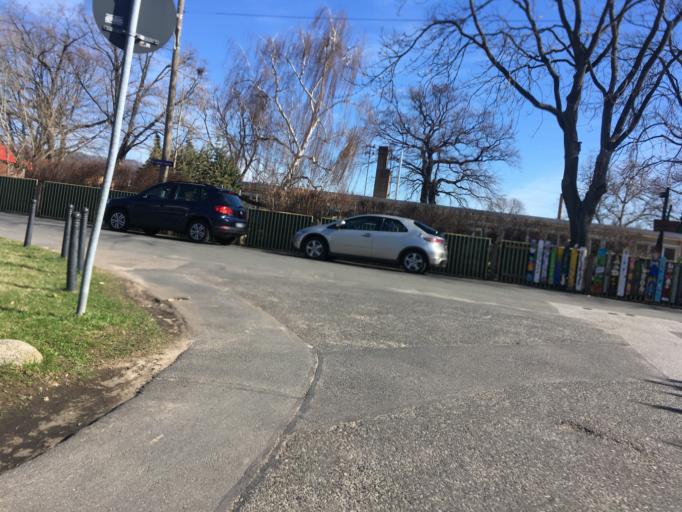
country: DE
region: Saxony
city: Radebeul
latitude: 51.0903
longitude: 13.6818
